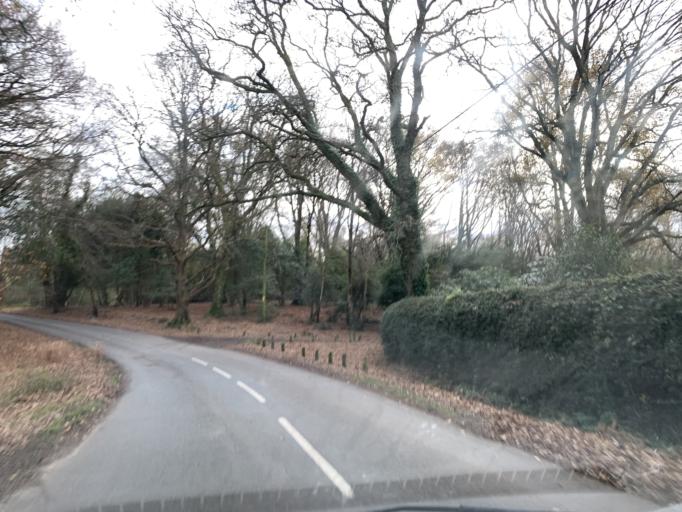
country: GB
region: England
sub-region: Hampshire
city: Lyndhurst
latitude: 50.8790
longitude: -1.6014
